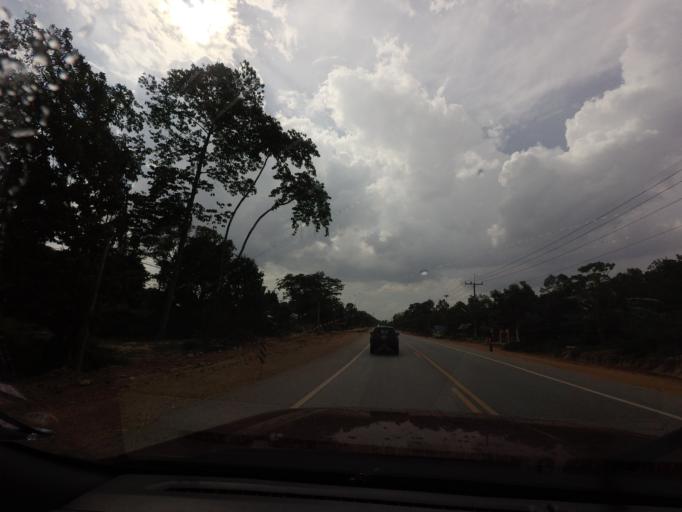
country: TH
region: Yala
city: Krong Pi Nang
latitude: 6.4041
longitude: 101.2815
